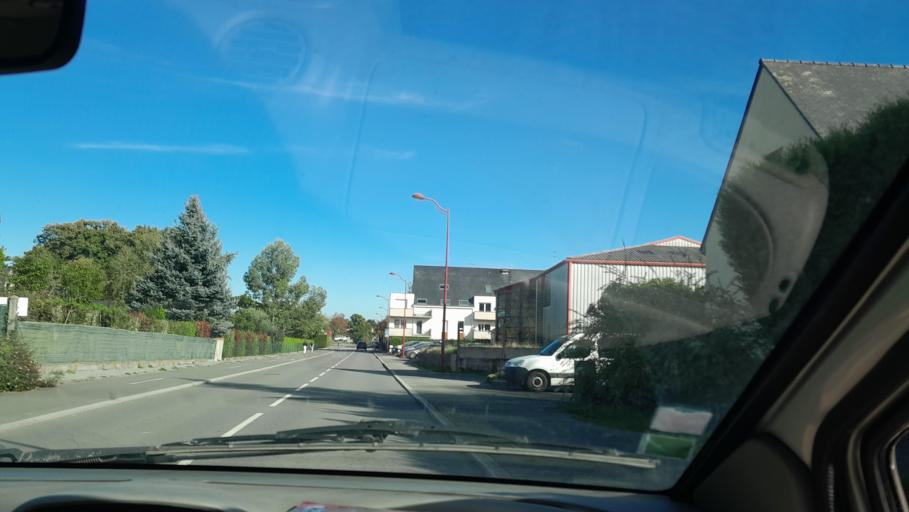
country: FR
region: Brittany
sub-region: Departement d'Ille-et-Vilaine
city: Etrelles
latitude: 48.0576
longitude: -1.1912
